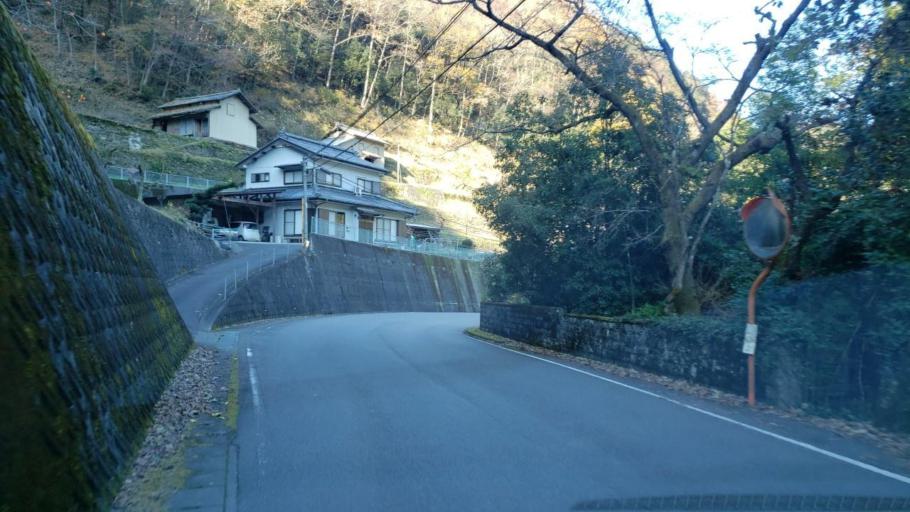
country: JP
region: Tokushima
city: Wakimachi
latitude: 34.0155
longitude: 134.0332
